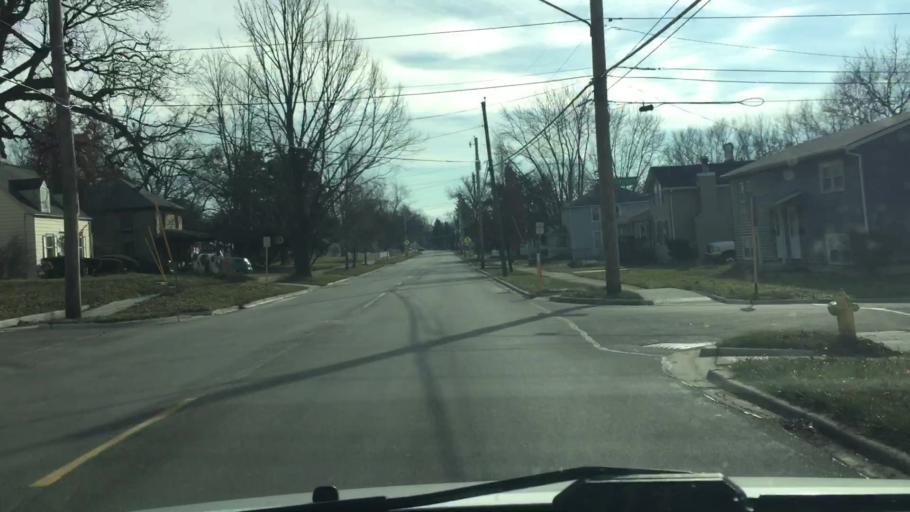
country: US
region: Illinois
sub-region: Kane County
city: Batavia
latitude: 41.8596
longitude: -88.3064
